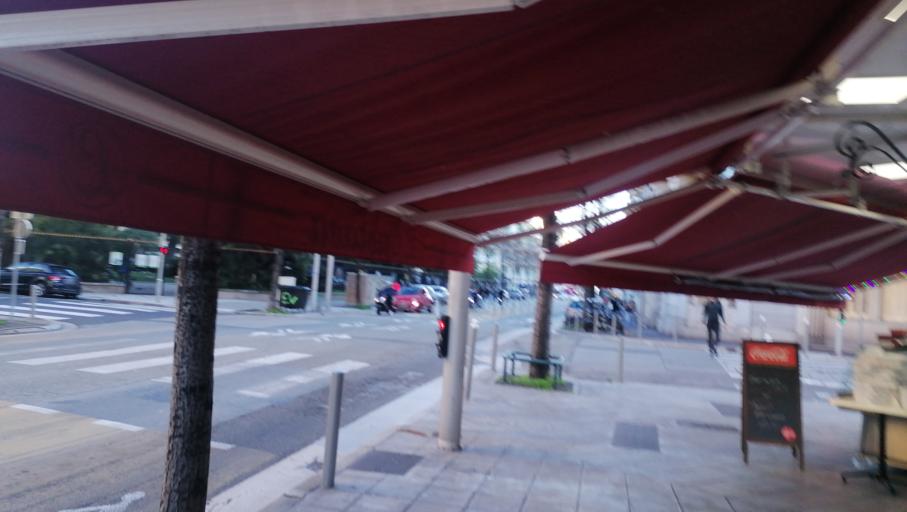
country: FR
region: Provence-Alpes-Cote d'Azur
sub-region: Departement des Alpes-Maritimes
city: Nice
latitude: 43.6992
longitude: 7.2563
